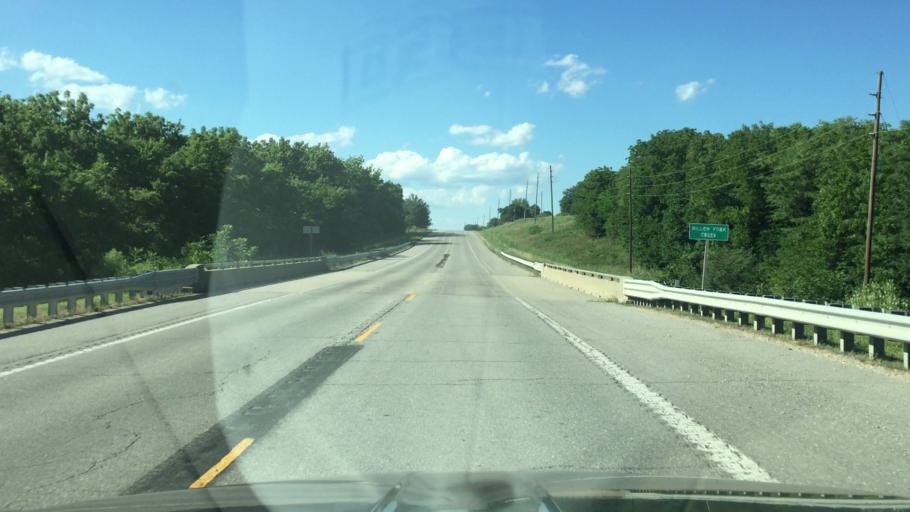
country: US
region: Missouri
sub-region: Moniteau County
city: Tipton
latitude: 38.6305
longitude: -92.7892
